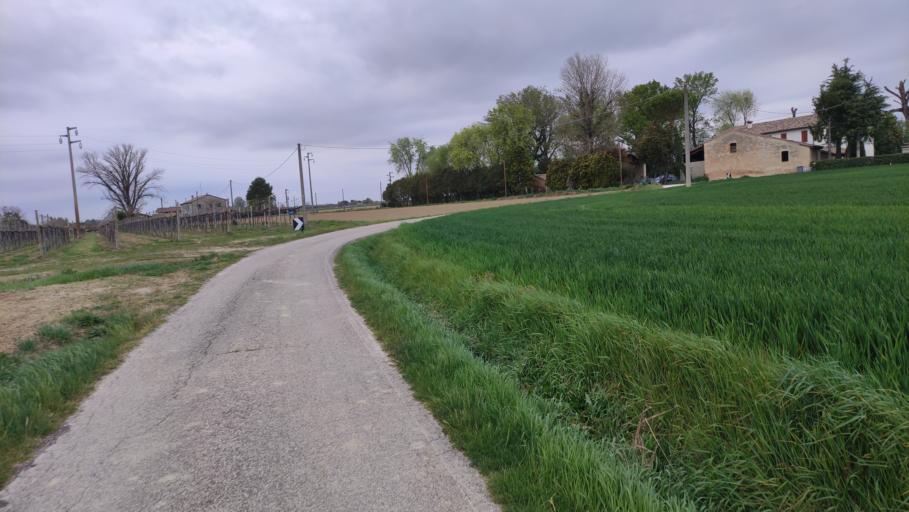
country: IT
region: Emilia-Romagna
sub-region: Provincia di Ravenna
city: Godo
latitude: 44.3947
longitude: 12.0509
